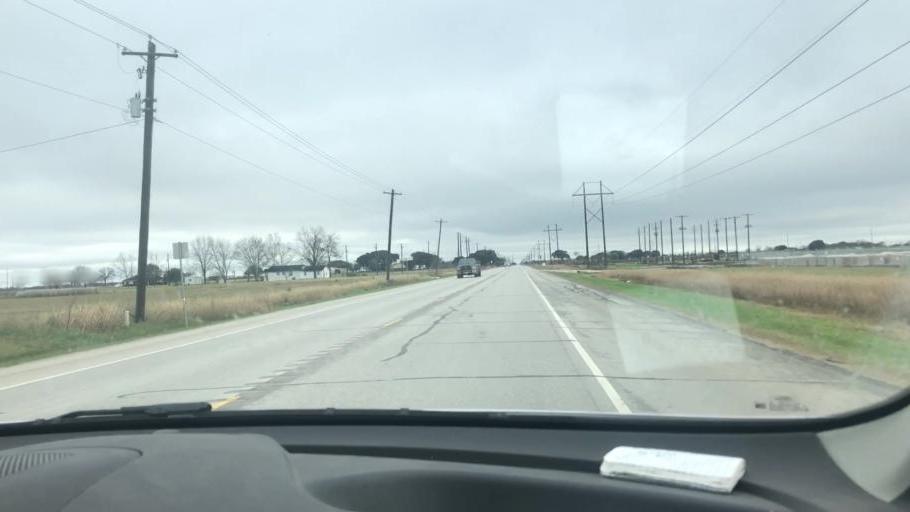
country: US
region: Texas
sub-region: Wharton County
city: Boling
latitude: 29.2077
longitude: -96.0248
